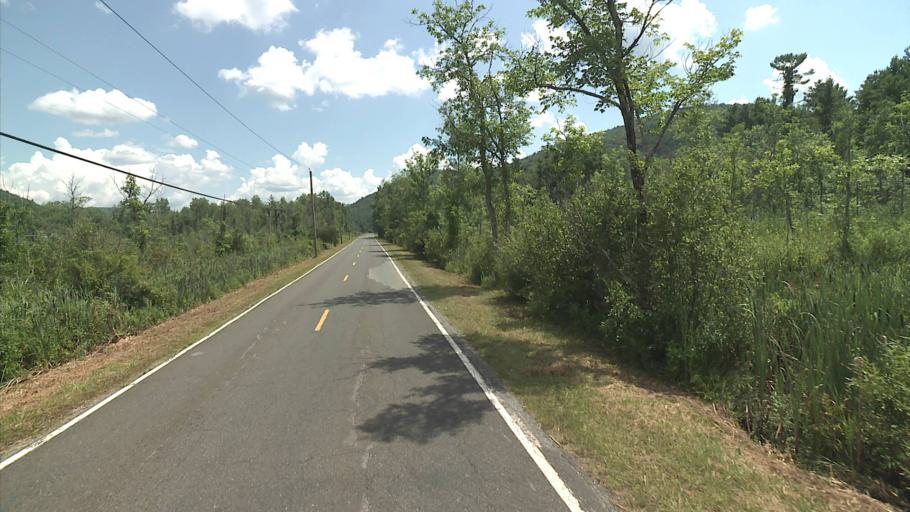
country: US
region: Connecticut
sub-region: Litchfield County
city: Canaan
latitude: 41.9505
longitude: -73.3389
